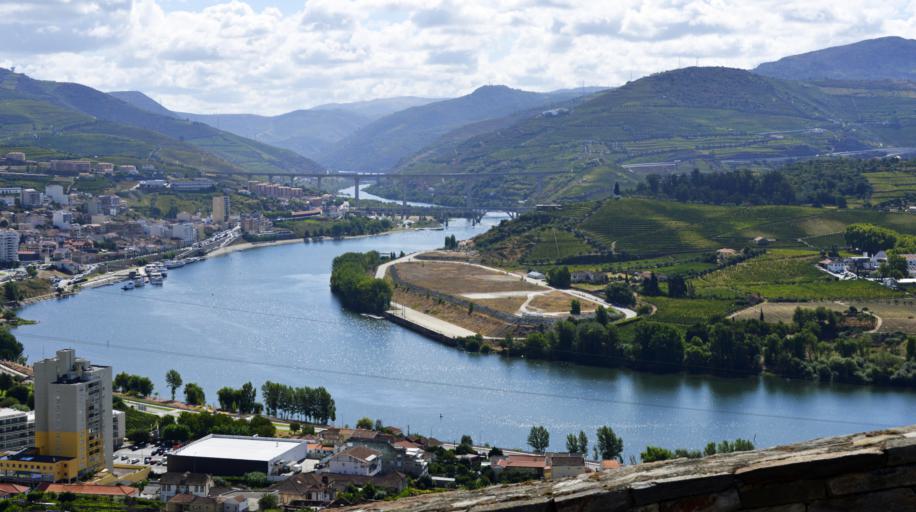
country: PT
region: Vila Real
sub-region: Peso da Regua
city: Godim
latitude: 41.1631
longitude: -7.8103
